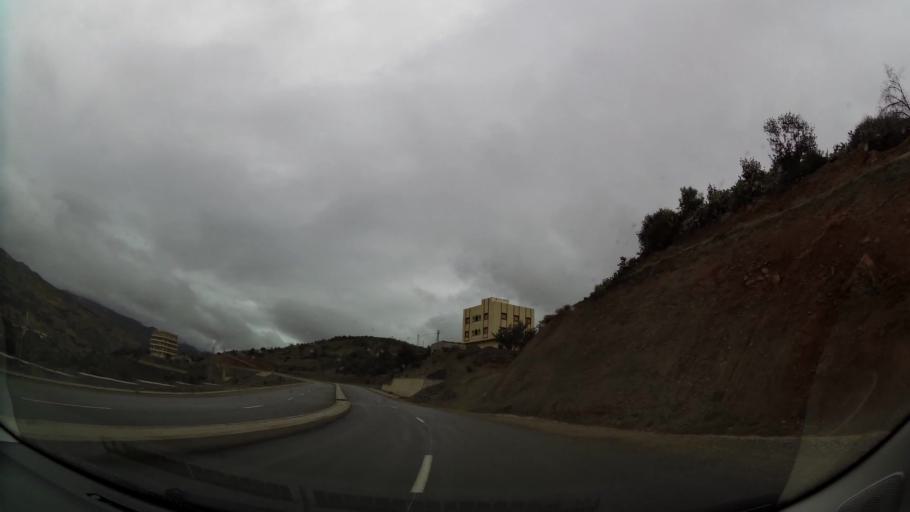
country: MA
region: Taza-Al Hoceima-Taounate
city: Imzourene
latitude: 34.9837
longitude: -3.8114
